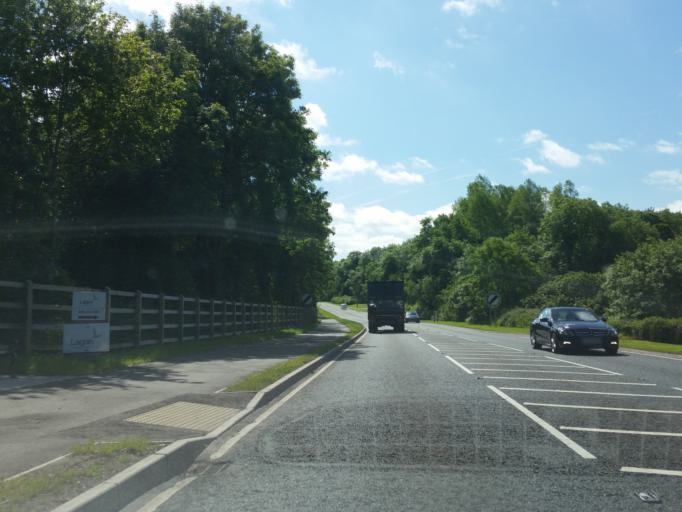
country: GB
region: Northern Ireland
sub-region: Fermanagh District
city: Enniskillen
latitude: 54.3282
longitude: -7.6166
